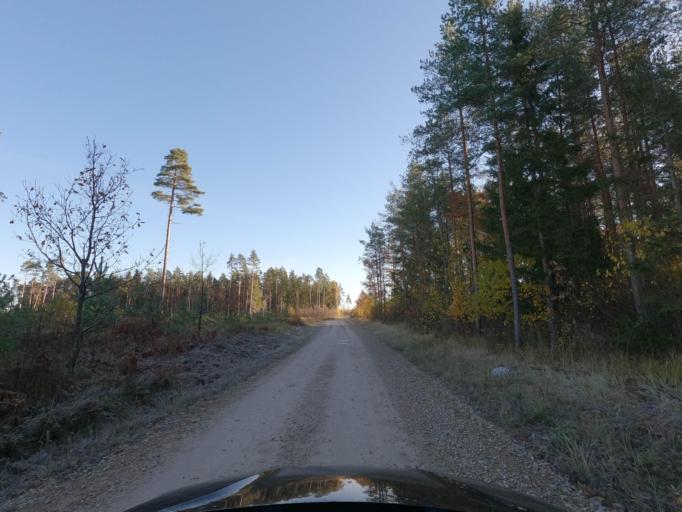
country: EE
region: Raplamaa
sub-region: Kohila vald
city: Kohila
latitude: 59.1248
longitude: 24.7705
